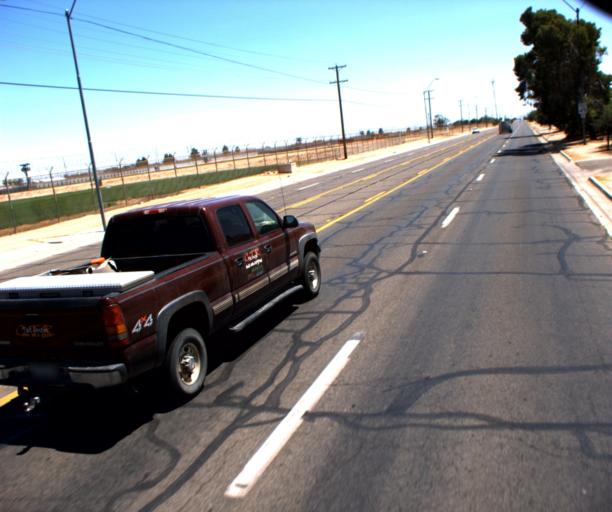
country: US
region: Arizona
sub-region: Pinal County
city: Florence
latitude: 33.0301
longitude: -111.3792
